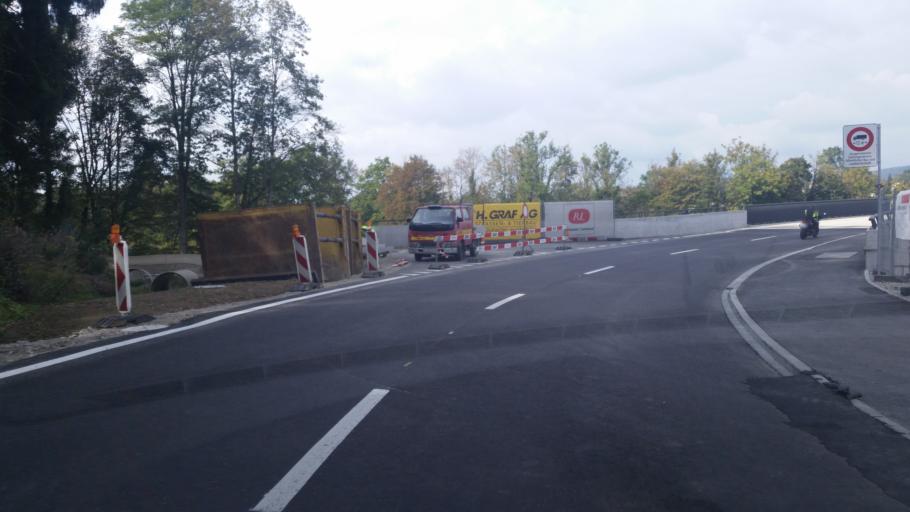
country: CH
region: Aargau
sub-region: Bezirk Baden
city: Kunten
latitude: 47.3932
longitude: 8.3017
